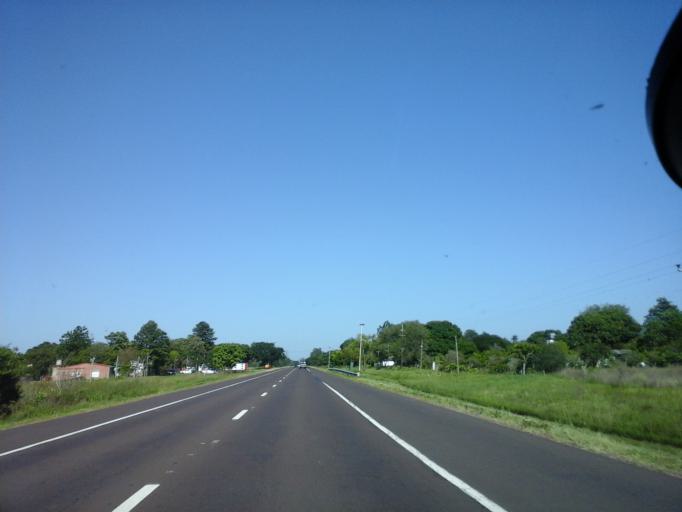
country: AR
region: Corrientes
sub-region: Departamento de San Cosme
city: San Cosme
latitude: -27.3673
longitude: -58.4258
